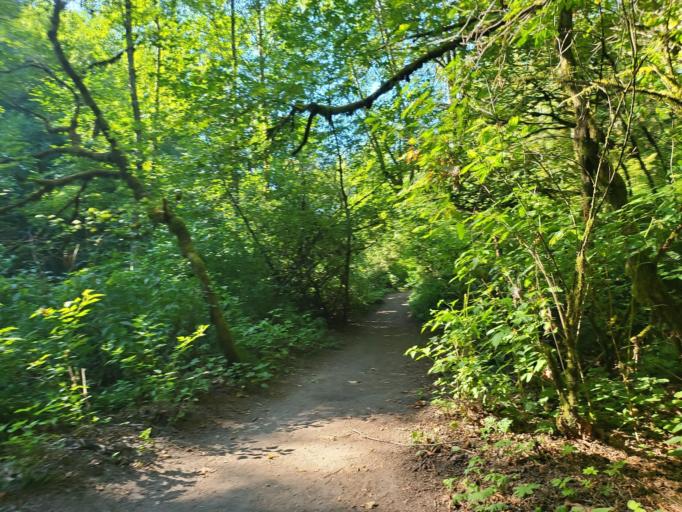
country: US
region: Washington
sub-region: King County
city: Newcastle
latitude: 47.5476
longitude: -122.1619
